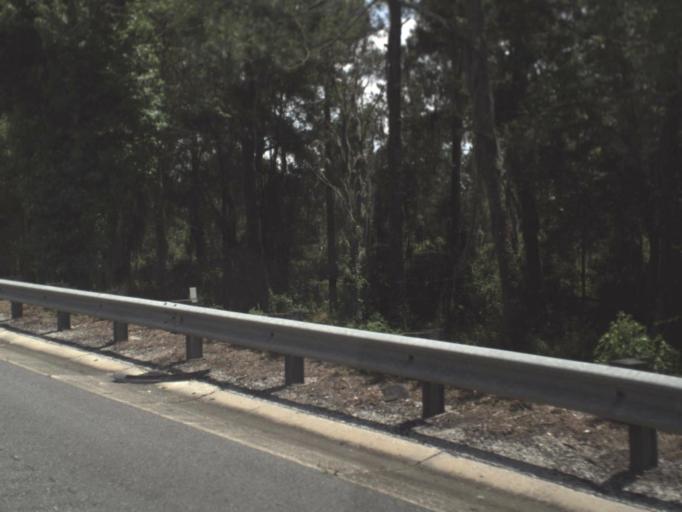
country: US
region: Florida
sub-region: Hamilton County
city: Jasper
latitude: 30.4587
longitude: -82.9498
